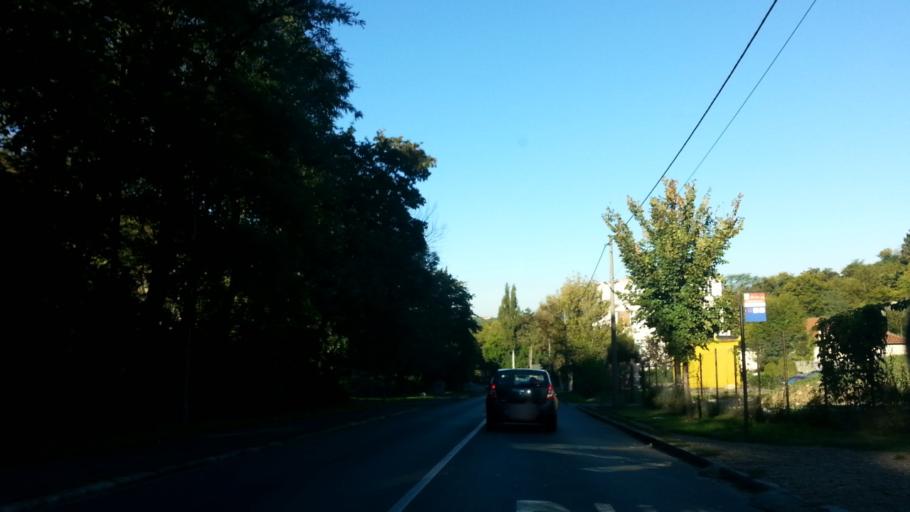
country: RS
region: Central Serbia
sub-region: Belgrade
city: Savski Venac
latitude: 44.7804
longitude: 20.4503
